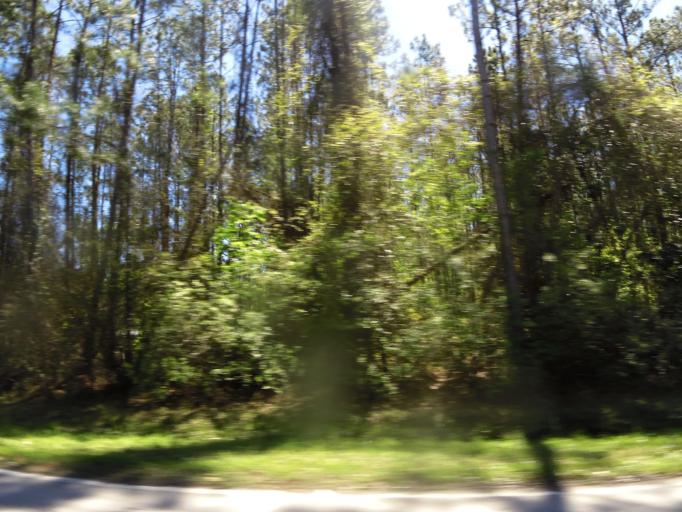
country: US
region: Florida
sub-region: Bradford County
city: Starke
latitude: 30.0559
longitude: -82.0648
